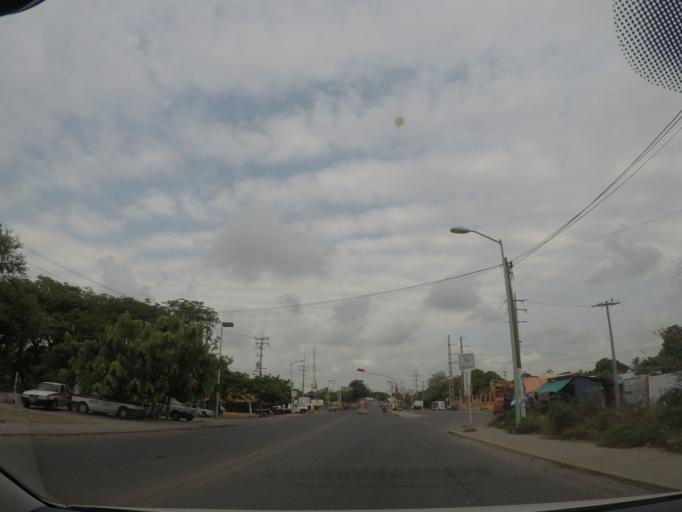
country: MX
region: Oaxaca
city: Juchitan de Zaragoza
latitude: 16.4474
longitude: -95.0165
